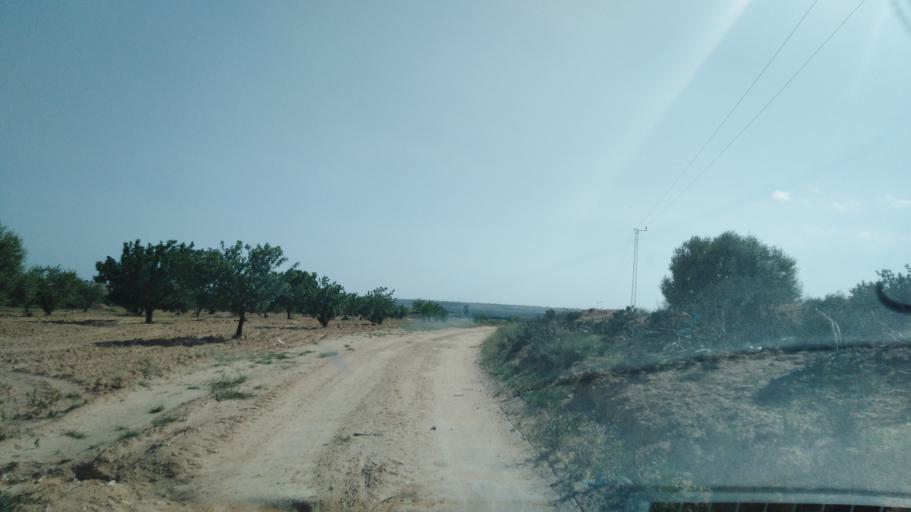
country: TN
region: Safaqis
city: Bi'r `Ali Bin Khalifah
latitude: 34.7946
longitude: 10.3728
